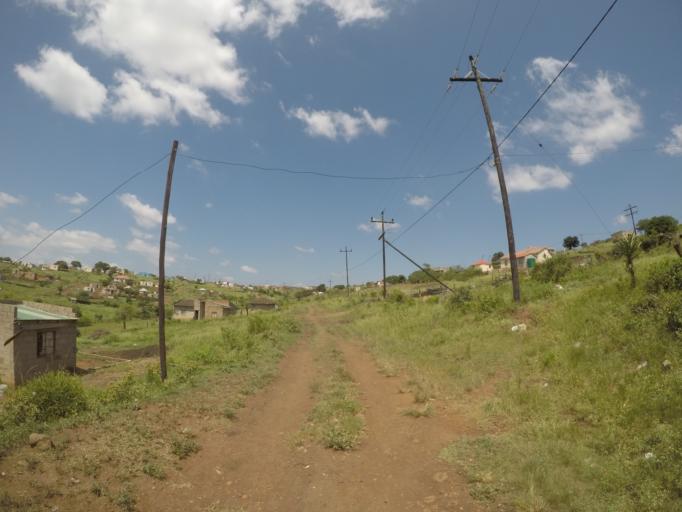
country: ZA
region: KwaZulu-Natal
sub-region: uThungulu District Municipality
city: Empangeni
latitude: -28.6069
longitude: 31.7347
